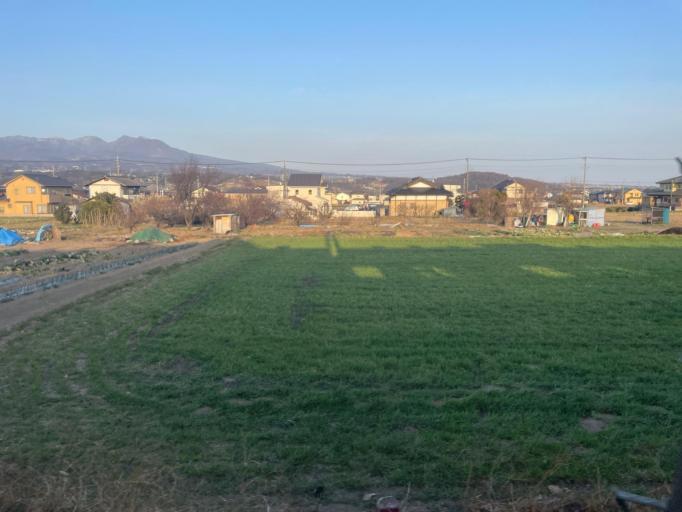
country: JP
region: Gunma
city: Shibukawa
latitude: 36.4567
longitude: 139.0206
